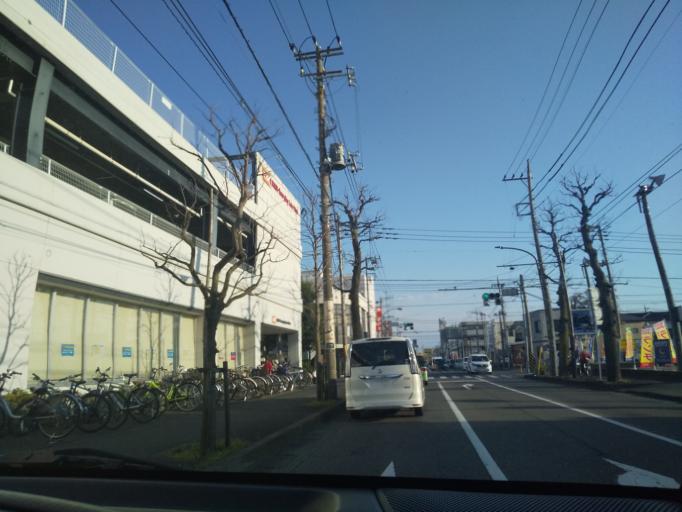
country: JP
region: Kanagawa
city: Zama
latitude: 35.5587
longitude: 139.3748
